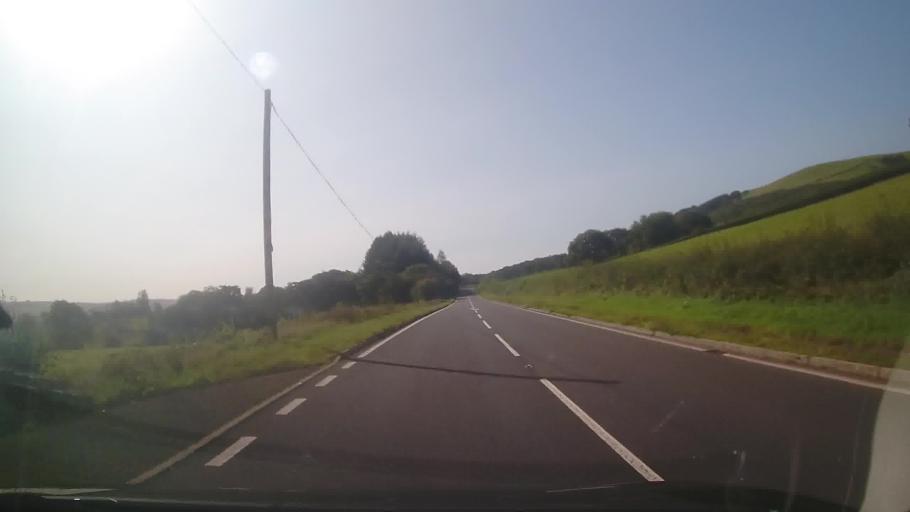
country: GB
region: Wales
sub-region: Sir Powys
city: Rhayader
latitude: 52.1313
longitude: -3.6131
